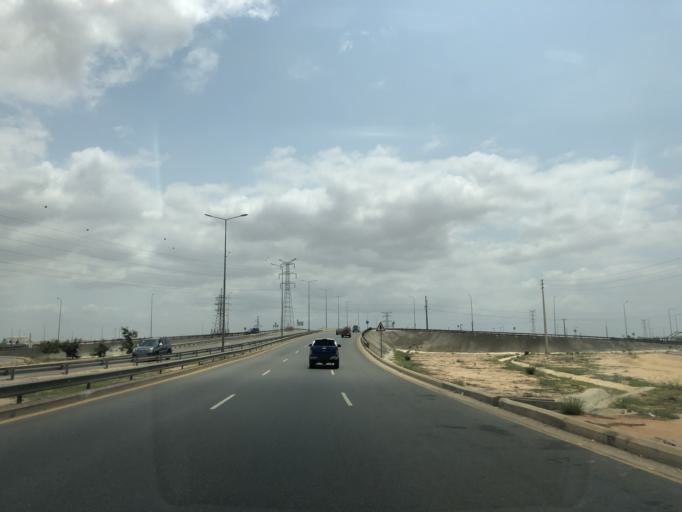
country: AO
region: Luanda
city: Luanda
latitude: -8.9707
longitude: 13.2545
